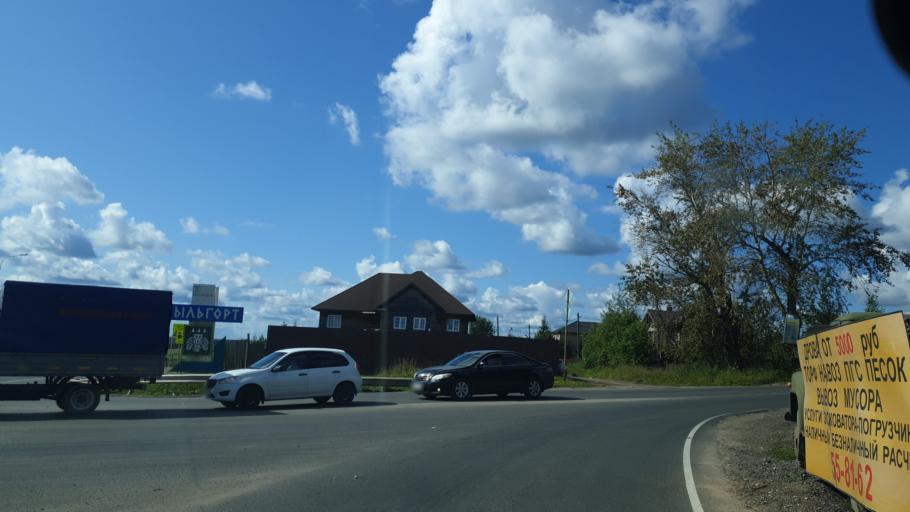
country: RU
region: Komi Republic
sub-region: Syktyvdinskiy Rayon
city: Syktyvkar
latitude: 61.6340
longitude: 50.8096
